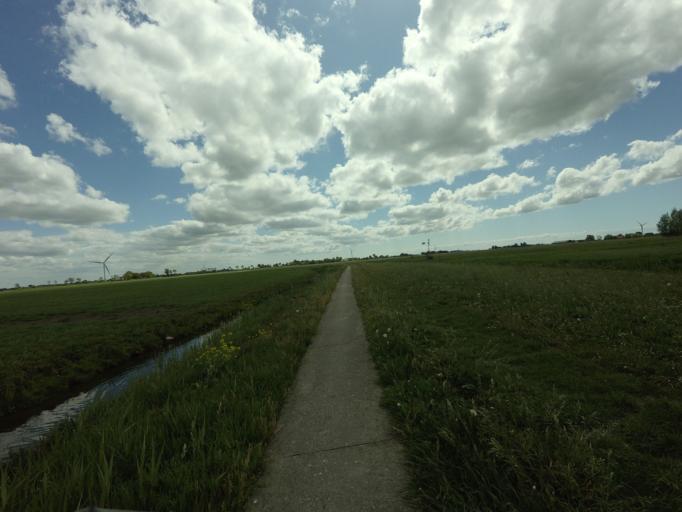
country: NL
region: Friesland
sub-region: Gemeente Littenseradiel
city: Wommels
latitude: 53.1321
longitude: 5.5736
